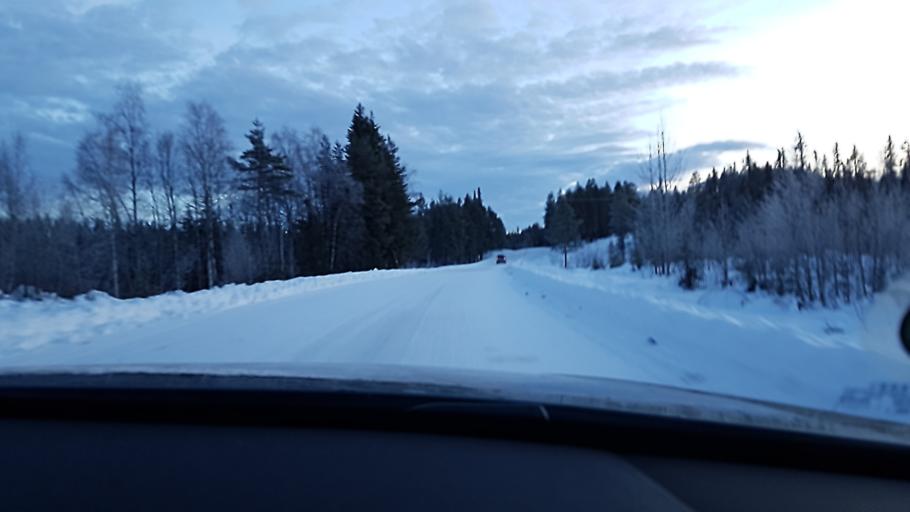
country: SE
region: Vaesterbotten
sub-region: Sorsele Kommun
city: Sorsele
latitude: 65.5016
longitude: 17.5532
